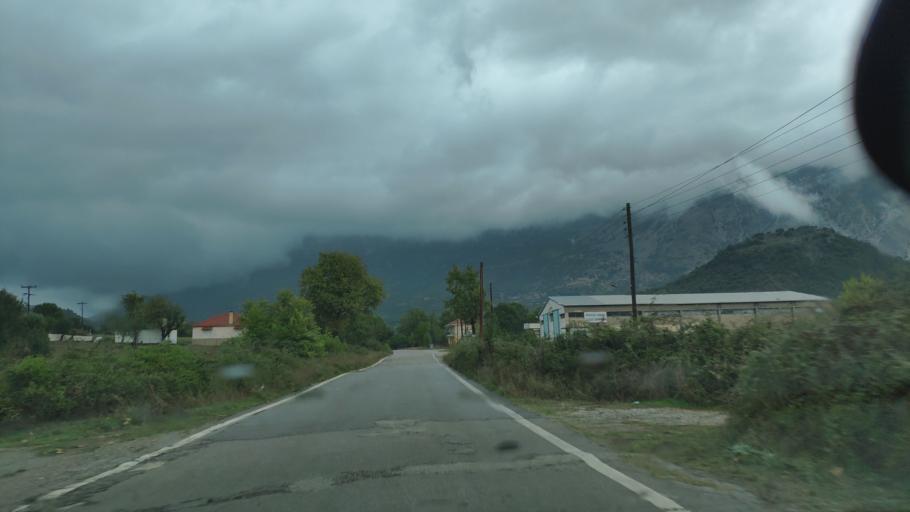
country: GR
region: West Greece
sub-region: Nomos Aitolias kai Akarnanias
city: Krikellos
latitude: 39.0086
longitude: 21.3097
